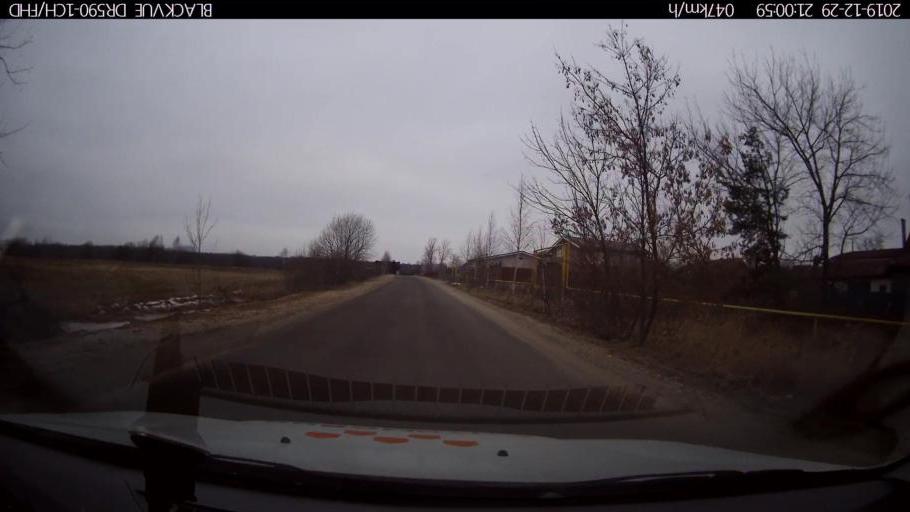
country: RU
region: Nizjnij Novgorod
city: Afonino
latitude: 56.1857
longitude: 43.9900
